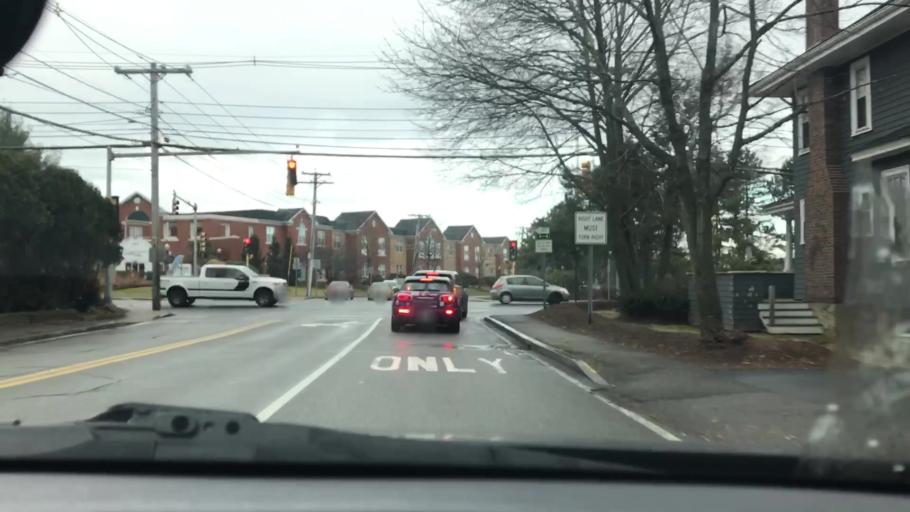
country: US
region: Massachusetts
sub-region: Norfolk County
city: Needham
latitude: 42.3002
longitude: -71.2287
